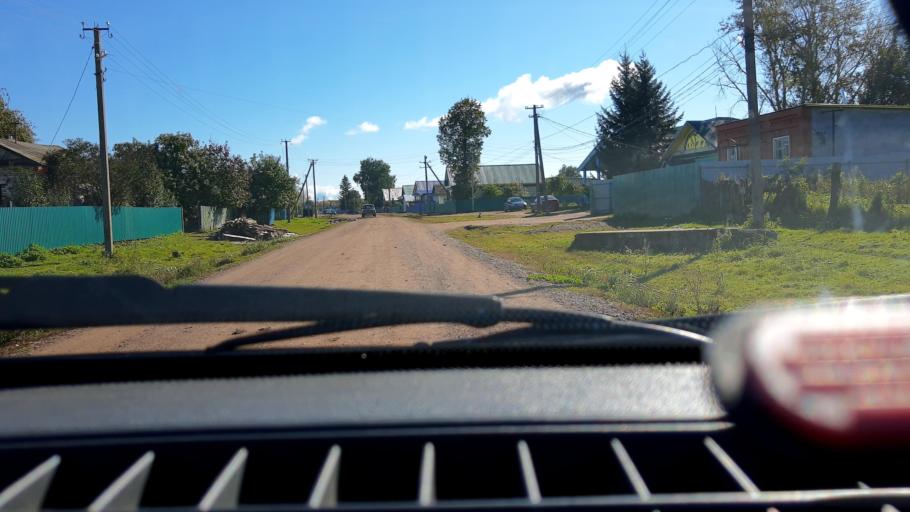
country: RU
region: Bashkortostan
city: Kushnarenkovo
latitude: 55.1152
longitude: 55.5411
